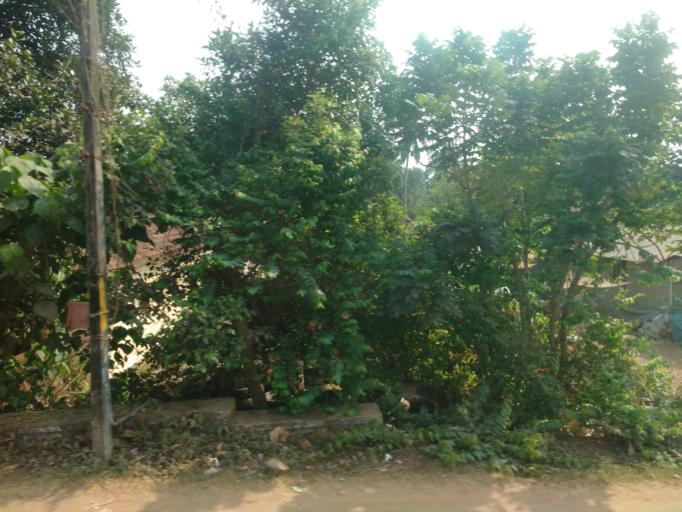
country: IN
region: Karnataka
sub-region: Dakshina Kannada
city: Mangalore
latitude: 12.8702
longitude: 74.8770
